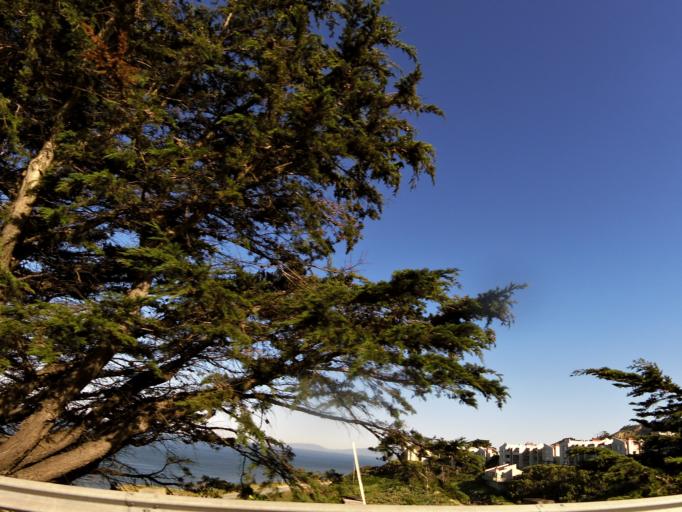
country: US
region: California
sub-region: San Mateo County
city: Broadmoor
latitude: 37.6579
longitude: -122.4902
